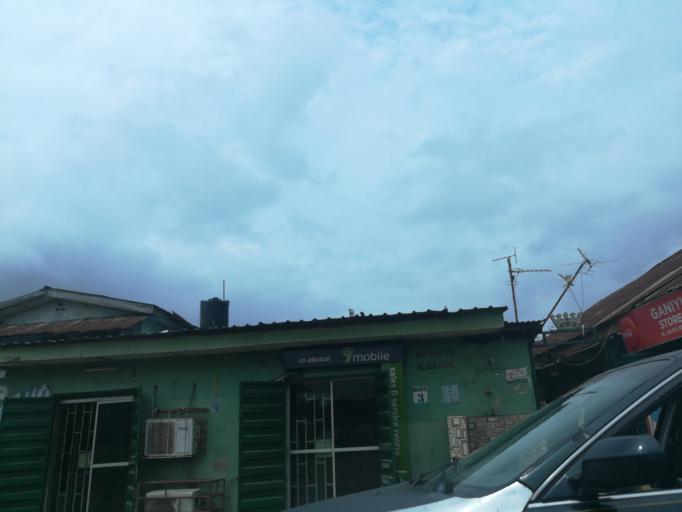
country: NG
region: Lagos
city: Ojota
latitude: 6.5719
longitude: 3.3623
